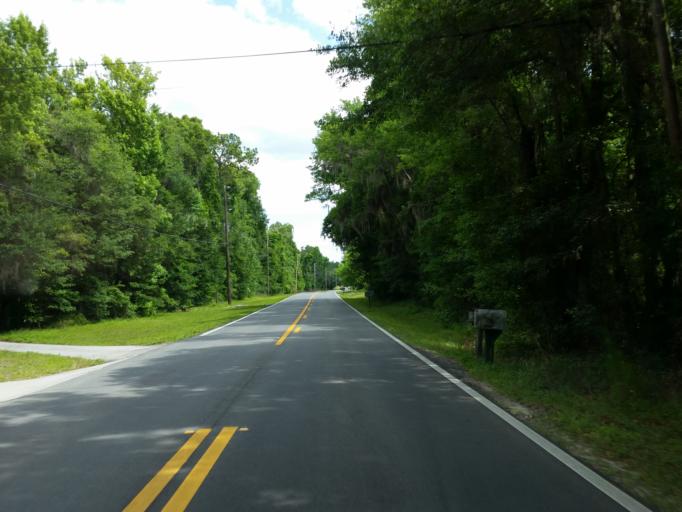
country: US
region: Florida
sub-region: Hernando County
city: North Brooksville
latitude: 28.6508
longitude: -82.3598
